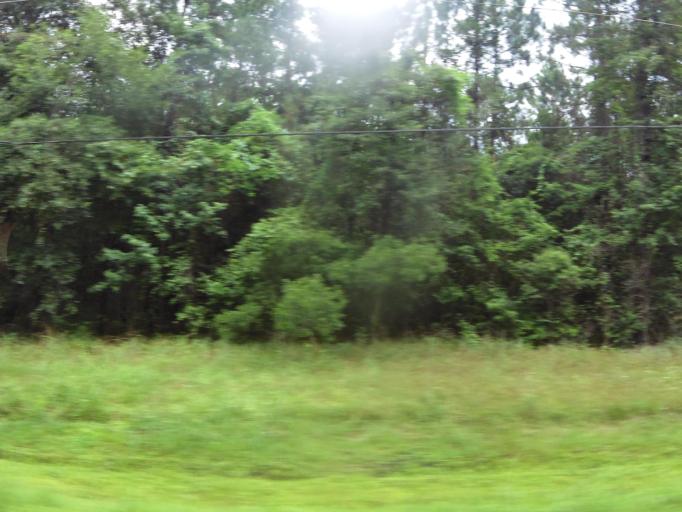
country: US
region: Florida
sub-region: Nassau County
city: Nassau Village-Ratliff
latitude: 30.4583
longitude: -81.7833
